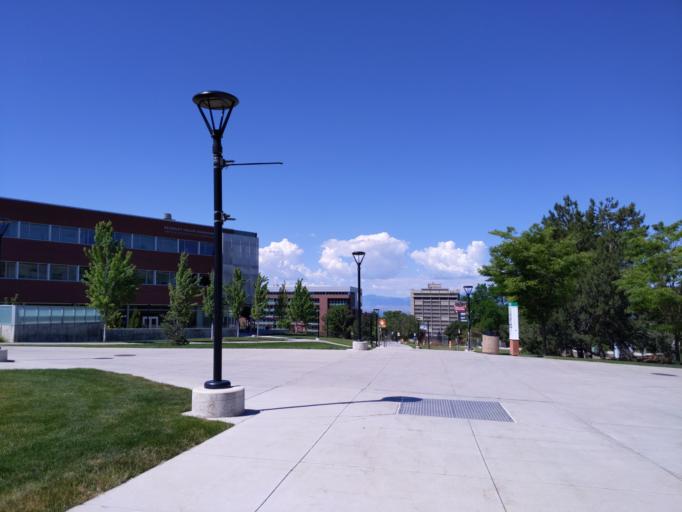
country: US
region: Utah
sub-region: Salt Lake County
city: Salt Lake City
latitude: 40.7638
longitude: -111.8415
